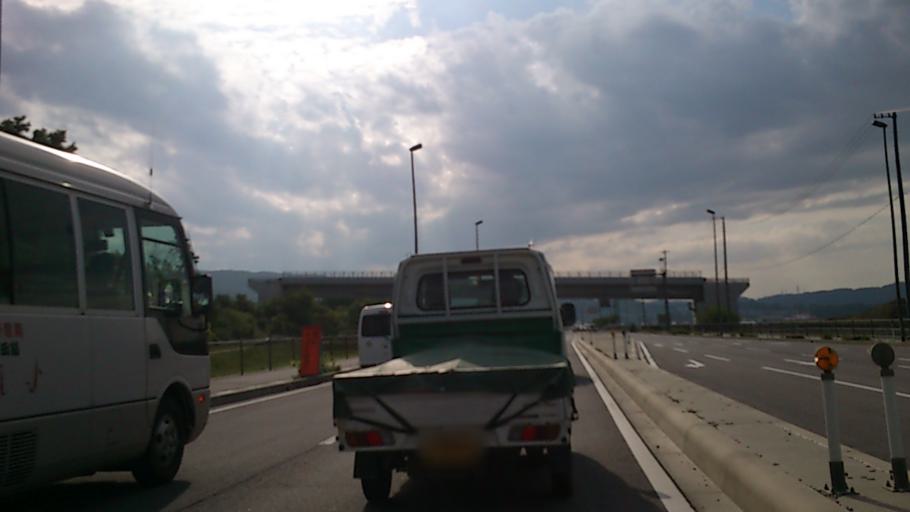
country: JP
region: Nagano
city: Saku
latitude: 36.2375
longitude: 138.4396
